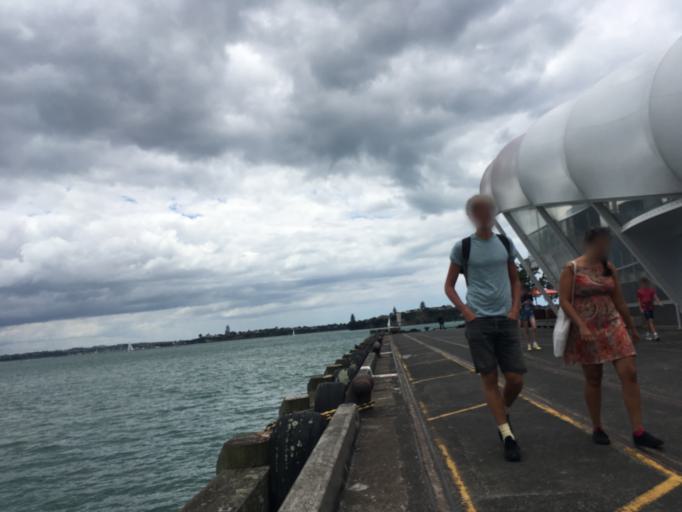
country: NZ
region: Auckland
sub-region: Auckland
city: Auckland
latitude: -36.8404
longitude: 174.7680
